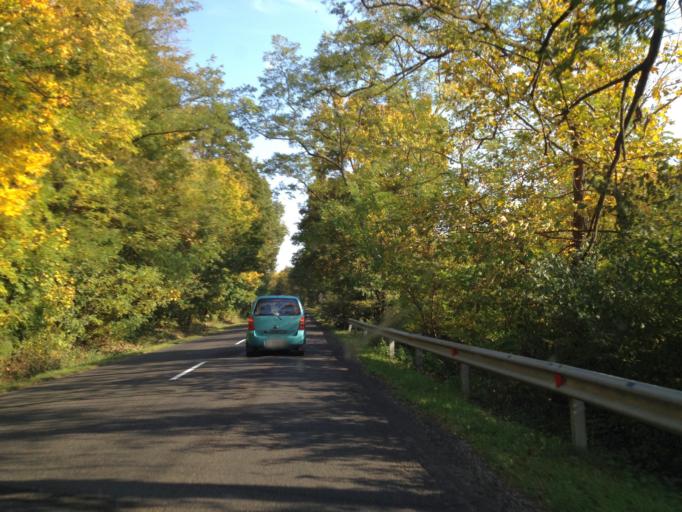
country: HU
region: Pest
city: Pilisszentkereszt
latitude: 47.6813
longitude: 18.9346
